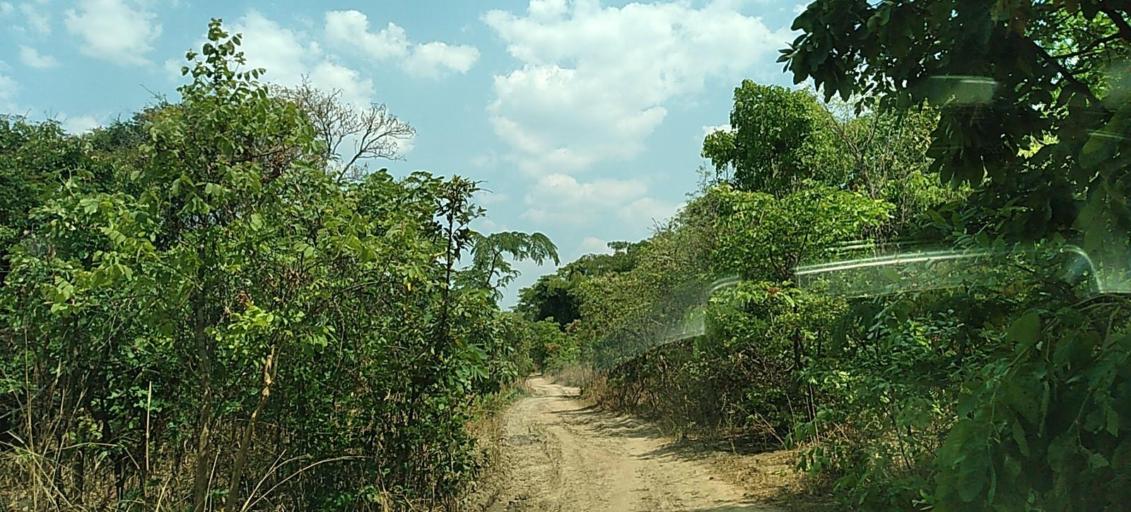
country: CD
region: Katanga
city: Kipushi
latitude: -12.0429
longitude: 27.4403
